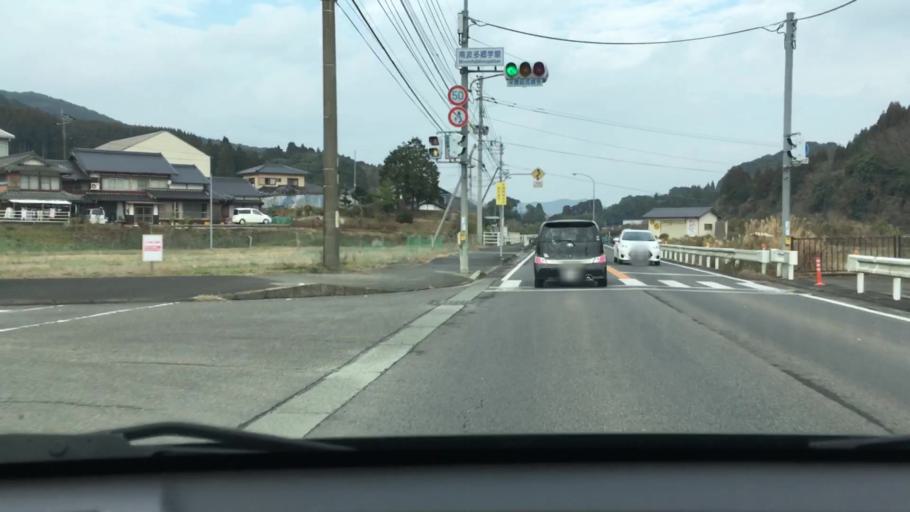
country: JP
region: Saga Prefecture
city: Imaricho-ko
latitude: 33.3171
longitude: 129.9290
